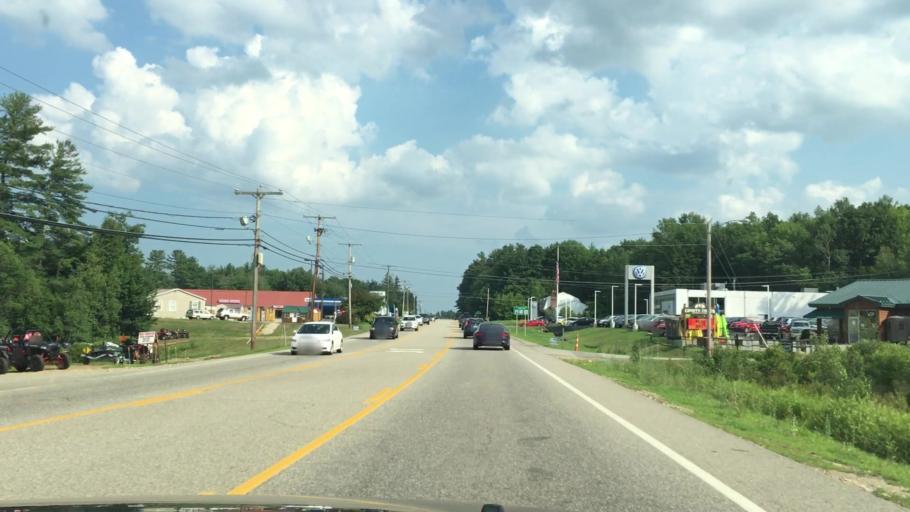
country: US
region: New Hampshire
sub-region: Strafford County
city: Rochester
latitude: 43.3253
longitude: -71.0021
